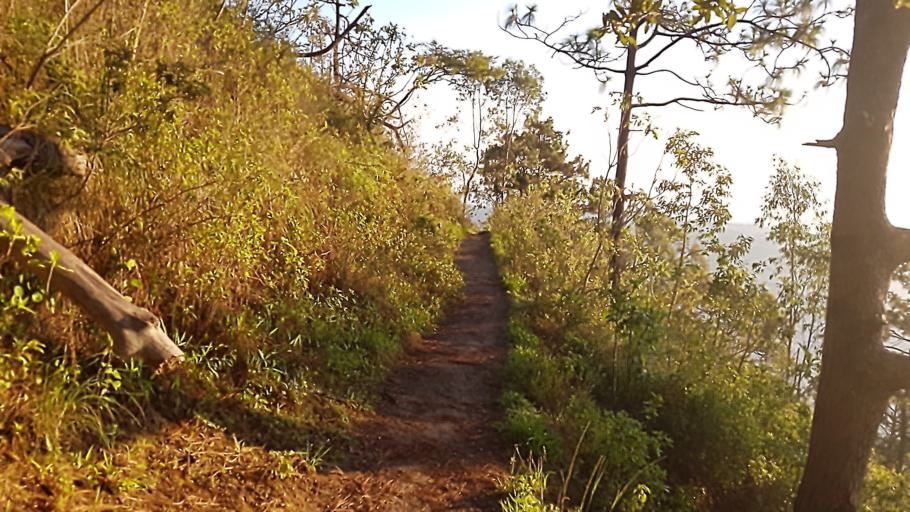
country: MX
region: Nayarit
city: Tepic
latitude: 21.5049
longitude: -104.9301
